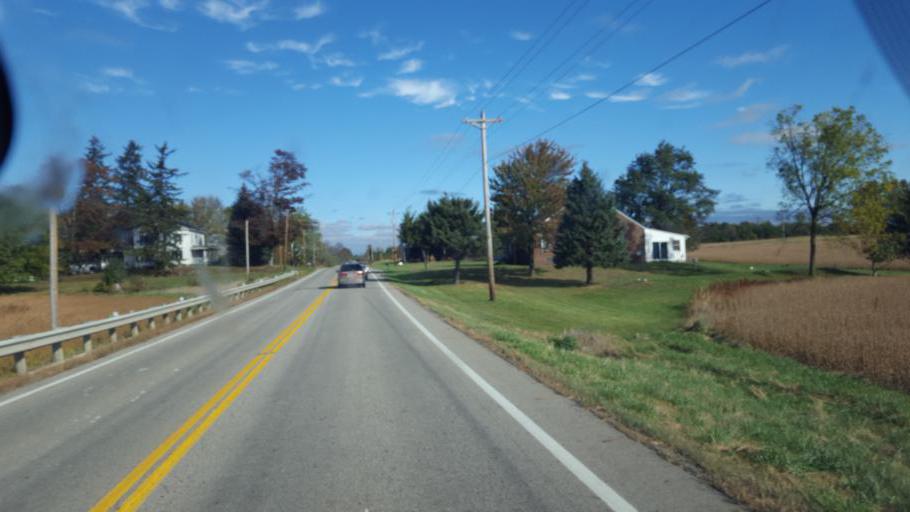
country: US
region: Ohio
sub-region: Huron County
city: Greenwich
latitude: 41.0678
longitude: -82.4869
